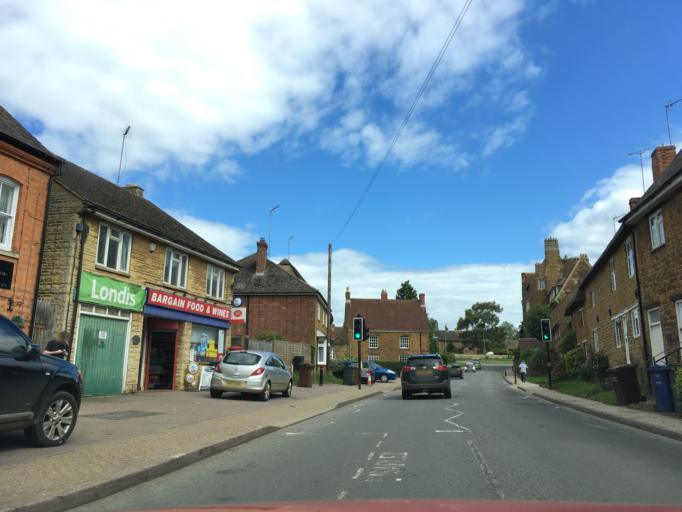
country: GB
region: England
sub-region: Oxfordshire
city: Bloxham
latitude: 52.0215
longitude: -1.3740
